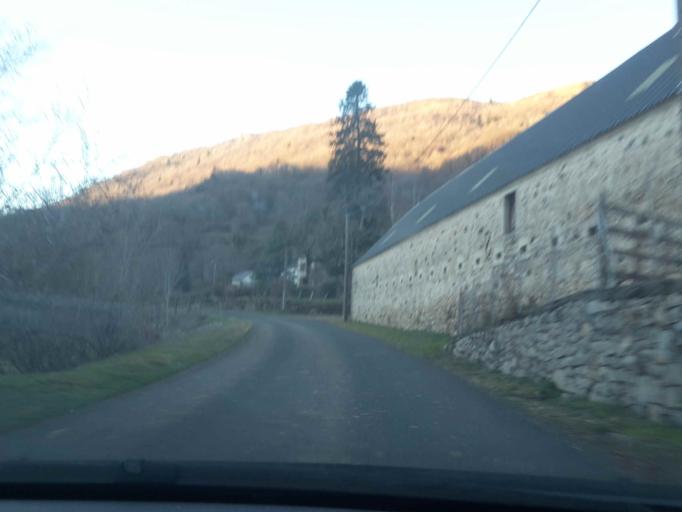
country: FR
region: Auvergne
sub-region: Departement du Cantal
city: Riom-es-Montagnes
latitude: 45.1875
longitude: 2.5734
